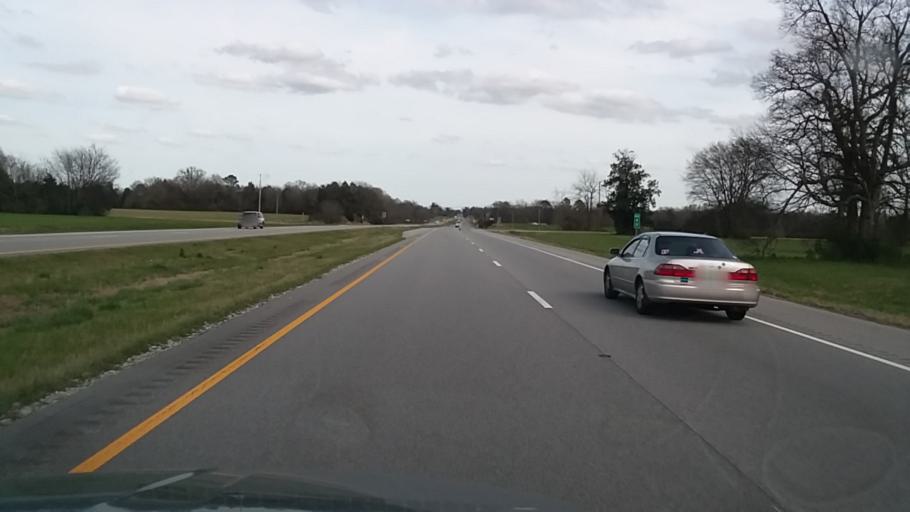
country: US
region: Alabama
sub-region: Lawrence County
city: Town Creek
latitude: 34.6824
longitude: -87.4607
